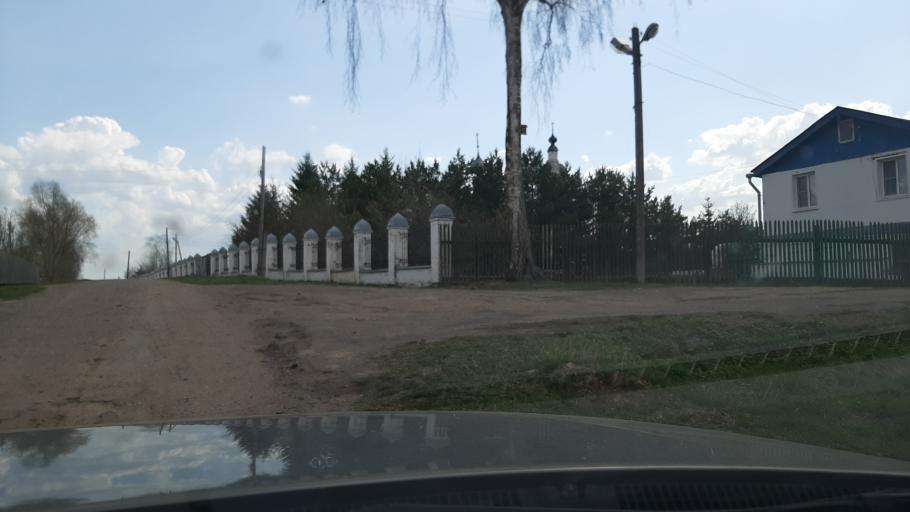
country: RU
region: Ivanovo
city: Privolzhsk
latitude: 57.3337
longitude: 41.2332
